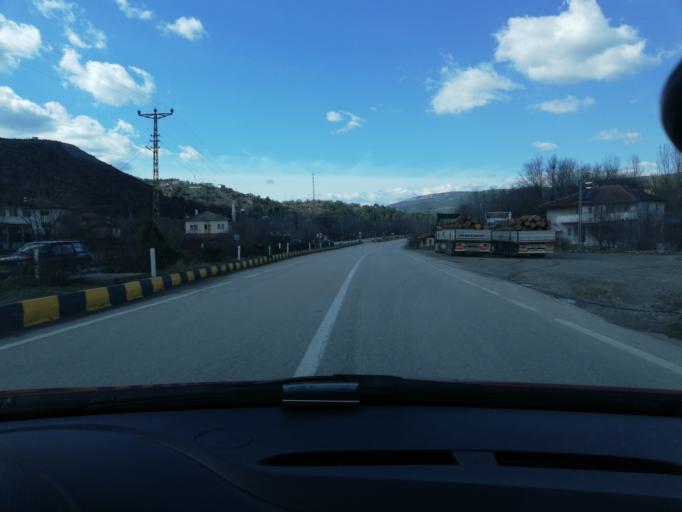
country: TR
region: Karabuk
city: Ovacik
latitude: 41.1975
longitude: 32.9153
